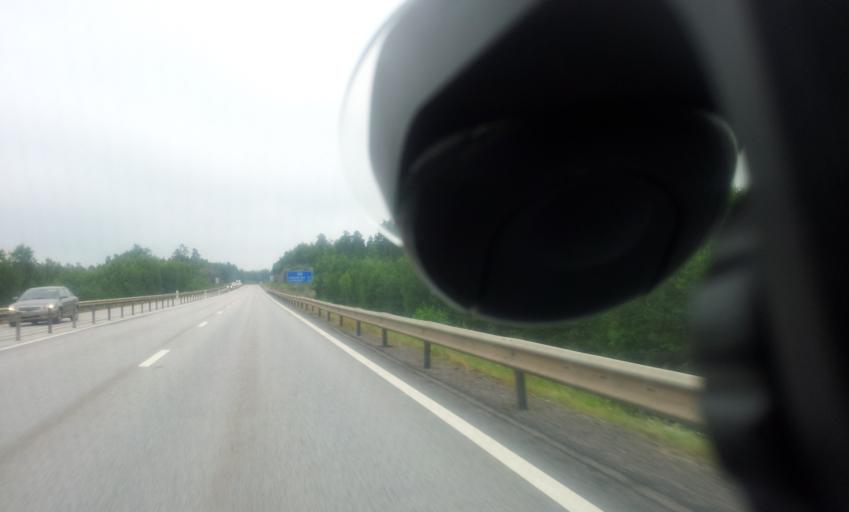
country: SE
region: Kalmar
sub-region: Vasterviks Kommun
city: Vaestervik
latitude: 57.7546
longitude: 16.5570
